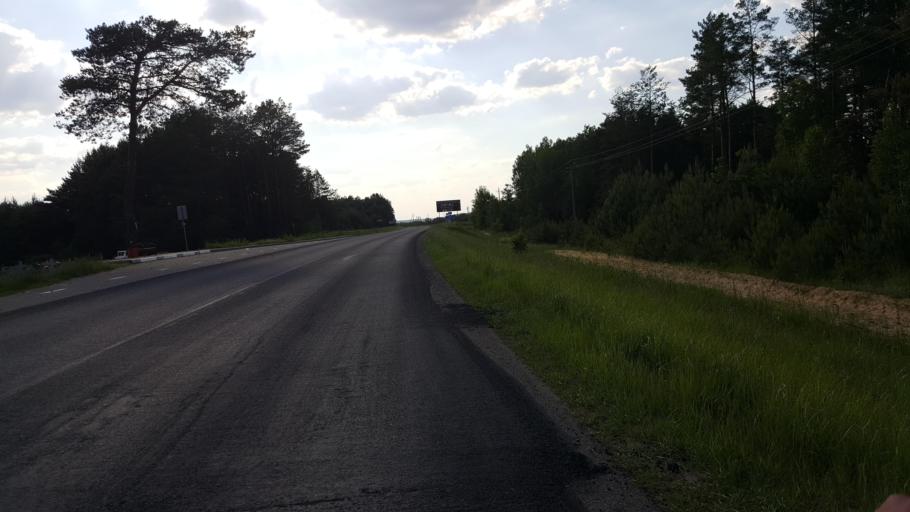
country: BY
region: Brest
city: Kamyanyets
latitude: 52.4001
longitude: 24.0094
